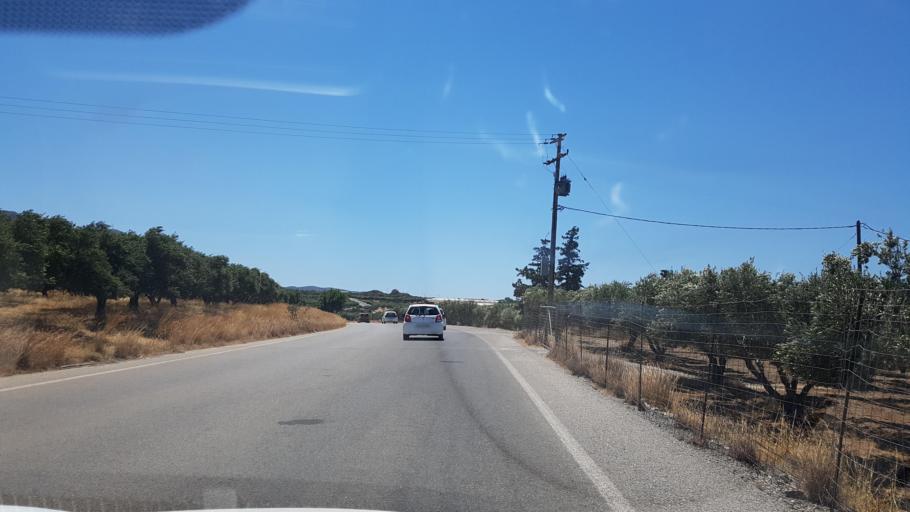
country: GR
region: Crete
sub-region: Nomos Chanias
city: Palaiochora
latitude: 35.2997
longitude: 23.5388
